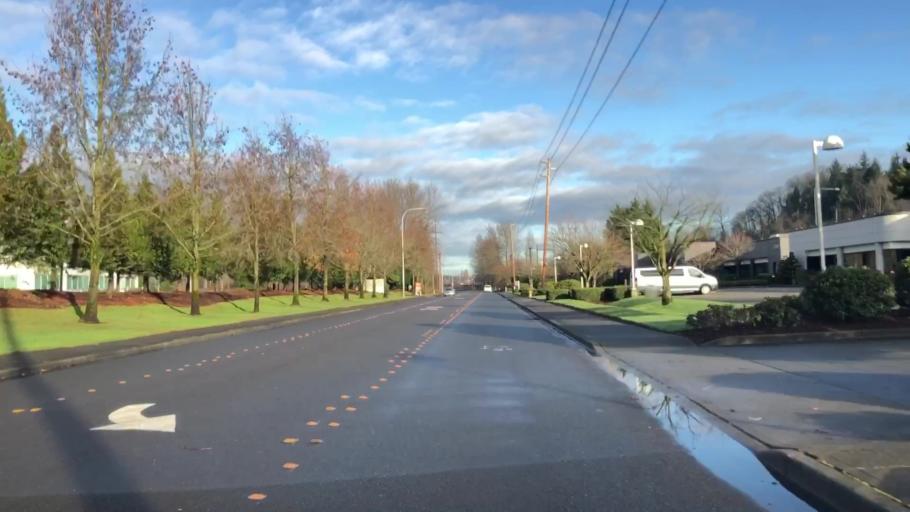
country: US
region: Washington
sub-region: King County
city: Renton
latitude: 47.4569
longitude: -122.2181
